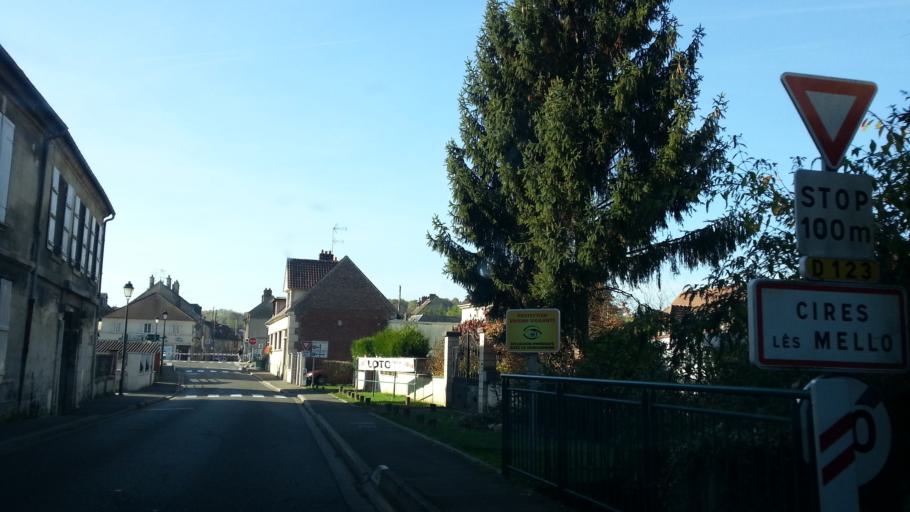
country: FR
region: Picardie
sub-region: Departement de l'Oise
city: Cires-les-Mello
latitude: 49.2727
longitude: 2.3617
